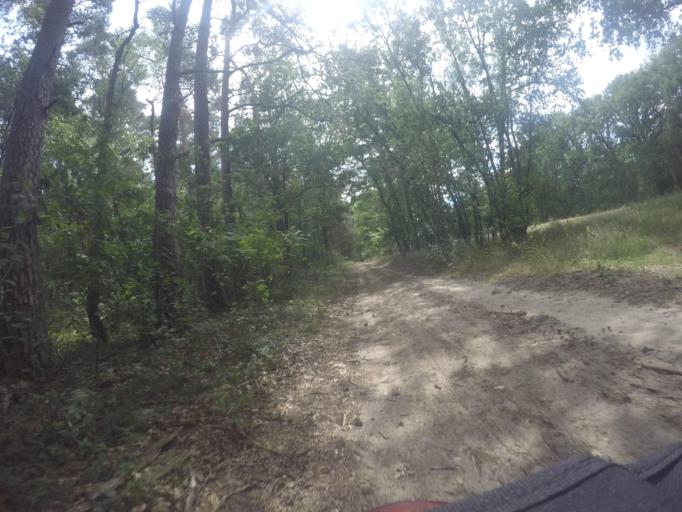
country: DE
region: Lower Saxony
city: Dahlenburg
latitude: 53.2144
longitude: 10.7153
